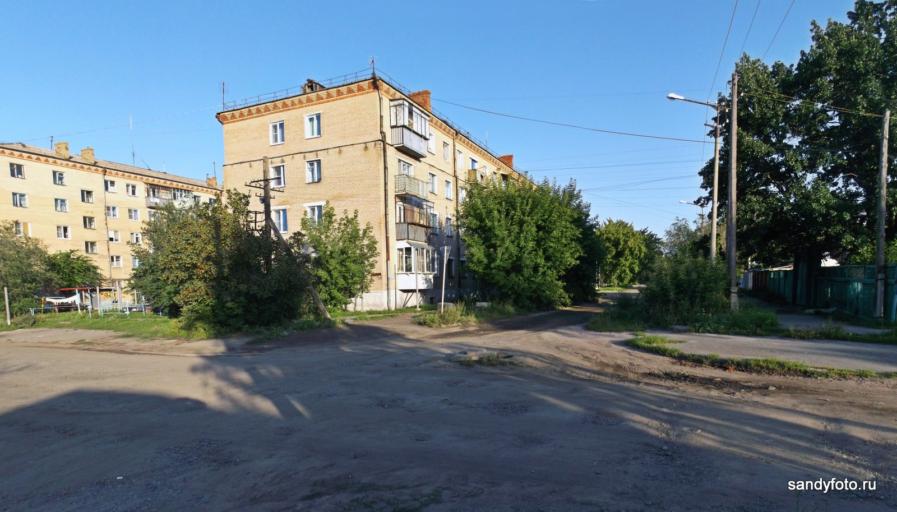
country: RU
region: Chelyabinsk
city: Troitsk
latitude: 54.0888
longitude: 61.5421
